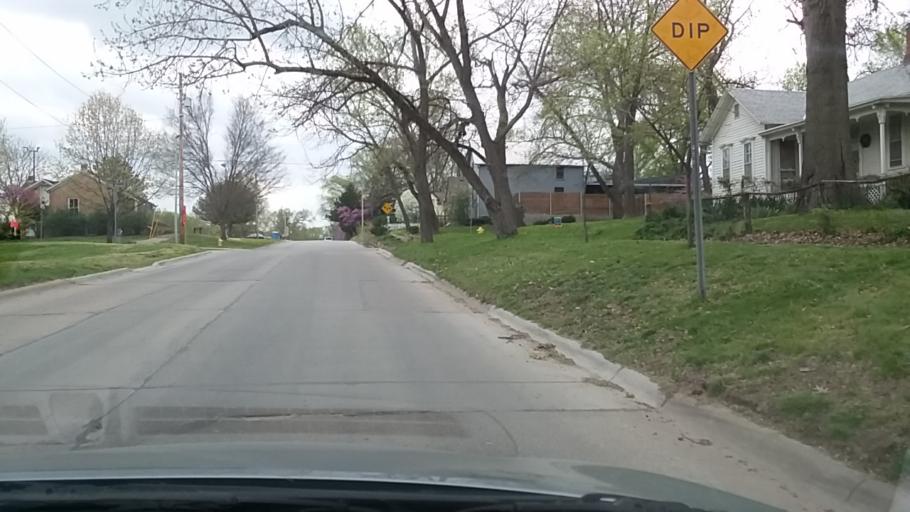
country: US
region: Kansas
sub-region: Douglas County
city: Lawrence
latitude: 38.9661
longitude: -95.2278
